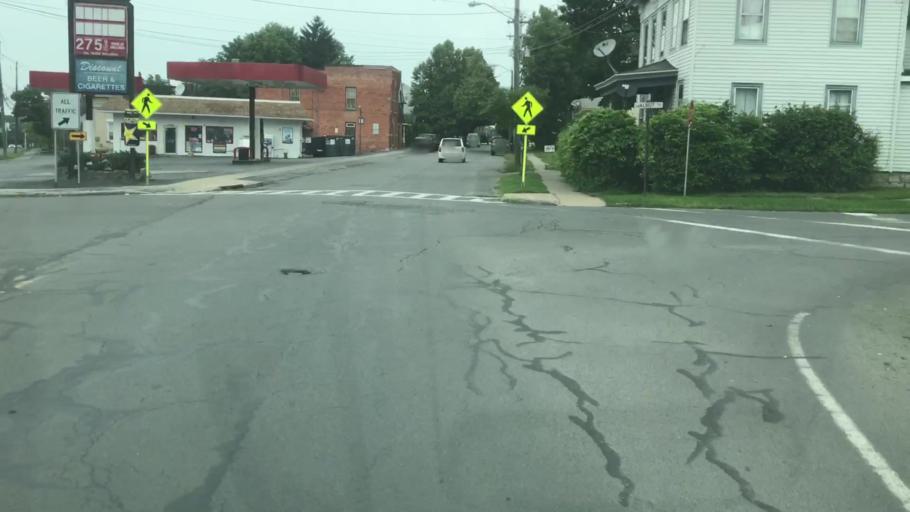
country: US
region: New York
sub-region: Cayuga County
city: Auburn
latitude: 42.9302
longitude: -76.5581
